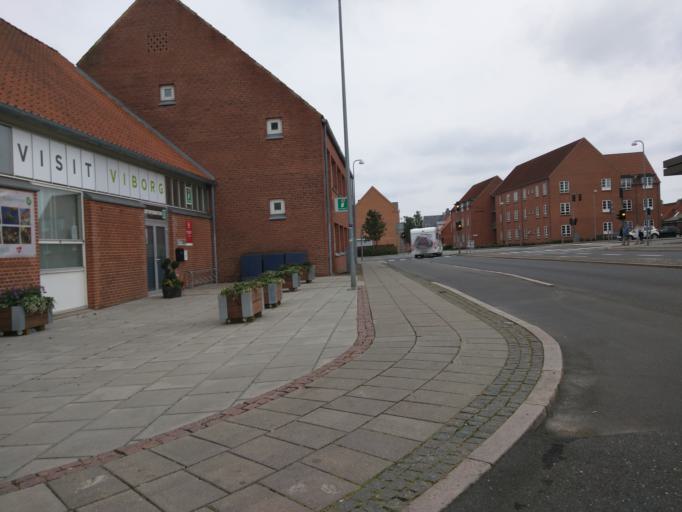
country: DK
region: Central Jutland
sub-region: Viborg Kommune
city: Viborg
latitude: 56.4536
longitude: 9.4035
